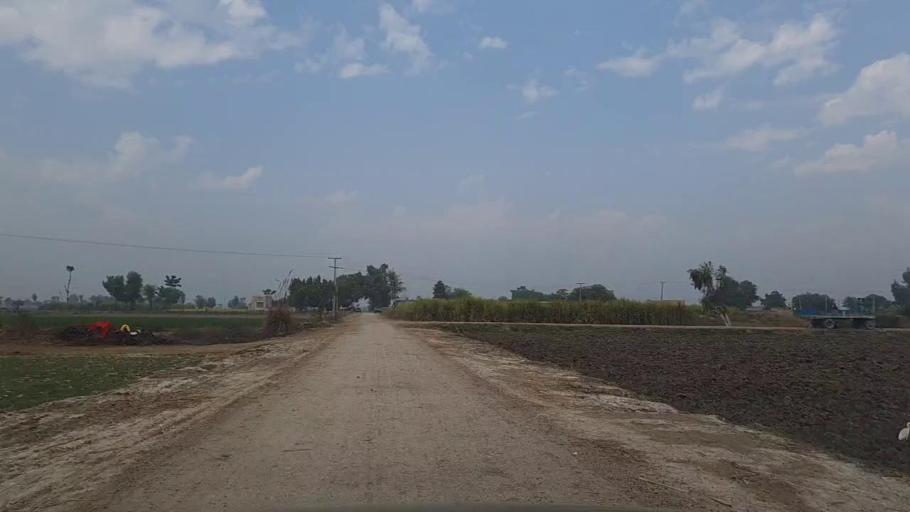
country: PK
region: Sindh
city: Daur
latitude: 26.3615
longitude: 68.3793
